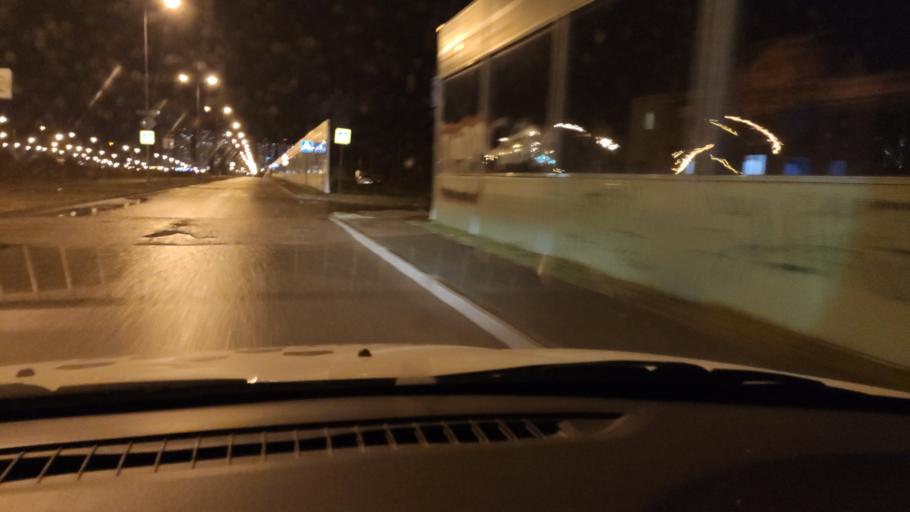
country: RU
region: Perm
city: Perm
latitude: 57.9934
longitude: 56.3043
